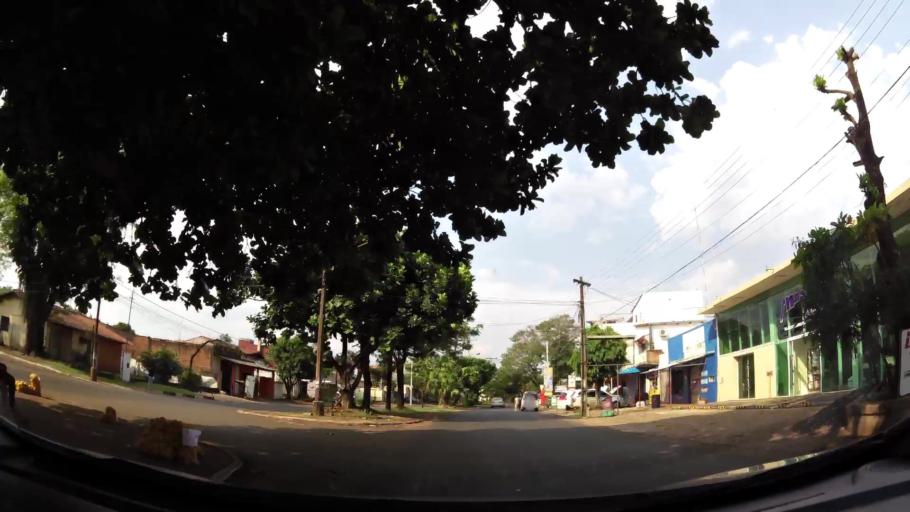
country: PY
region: Alto Parana
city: Presidente Franco
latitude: -25.5285
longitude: -54.6221
